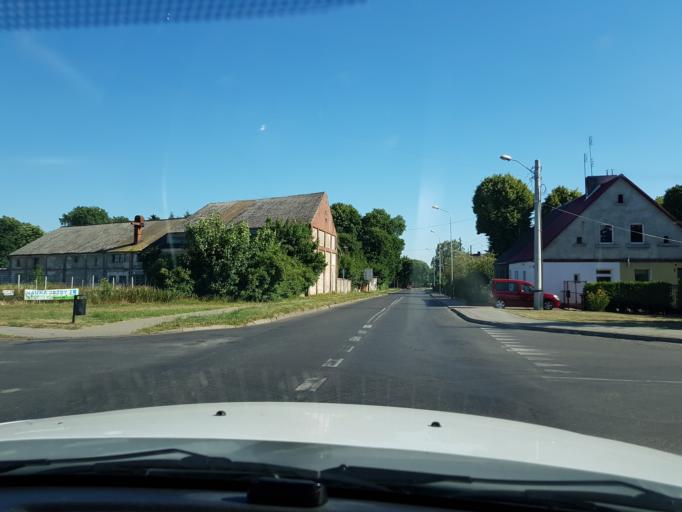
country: PL
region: West Pomeranian Voivodeship
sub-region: Powiat lobeski
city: Lobez
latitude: 53.6448
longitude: 15.6168
